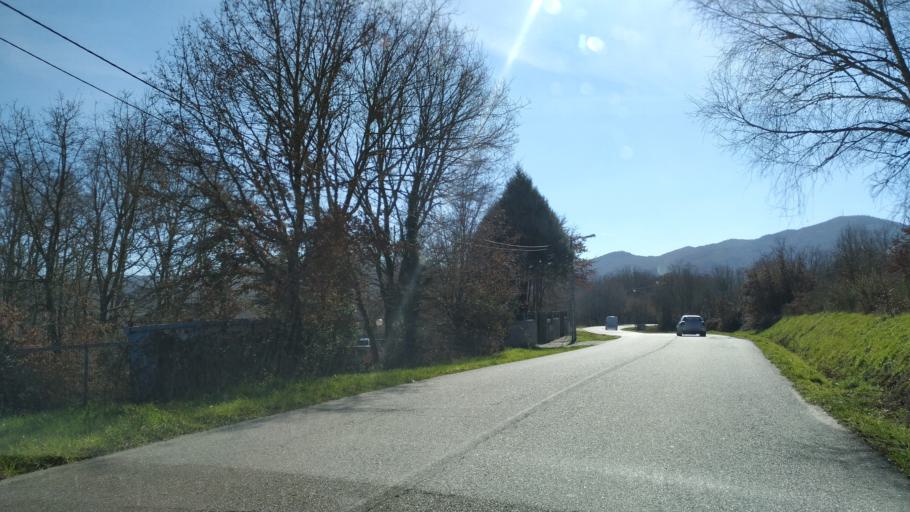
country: ES
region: Galicia
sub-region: Provincia de Ourense
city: Allariz
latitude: 42.2000
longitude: -7.8069
